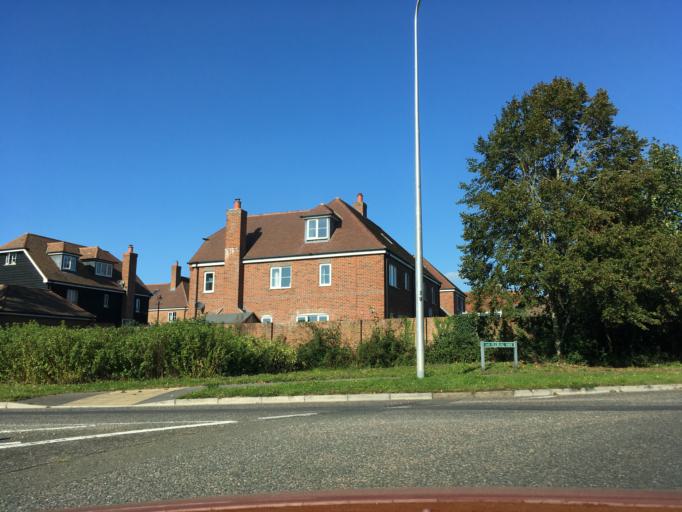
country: GB
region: England
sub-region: West Berkshire
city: Thatcham
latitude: 51.4089
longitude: -1.2459
